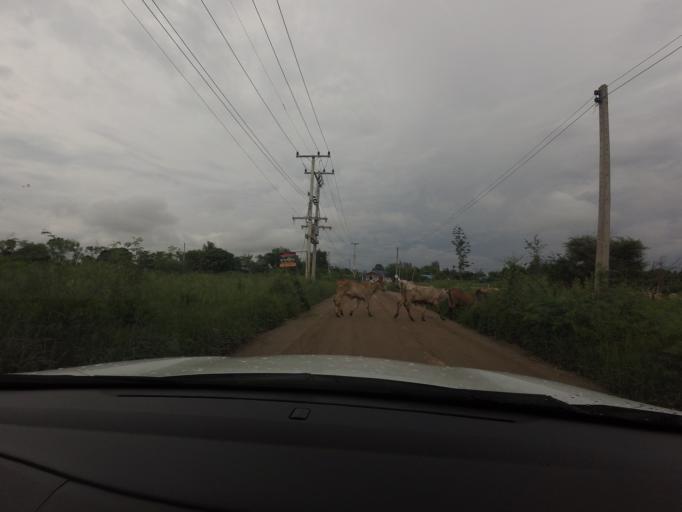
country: TH
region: Nakhon Ratchasima
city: Pak Chong
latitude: 14.6440
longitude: 101.4373
